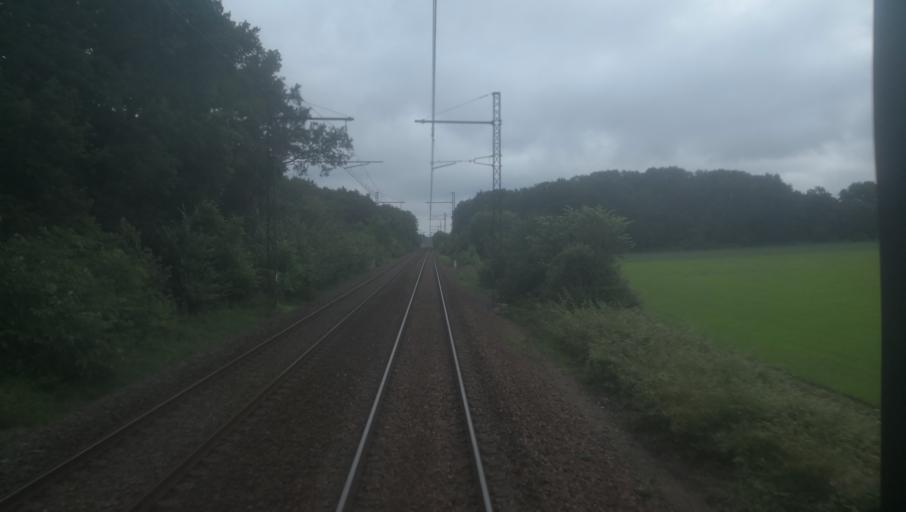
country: FR
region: Centre
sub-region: Departement du Cher
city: Mereau
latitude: 47.1626
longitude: 2.0570
